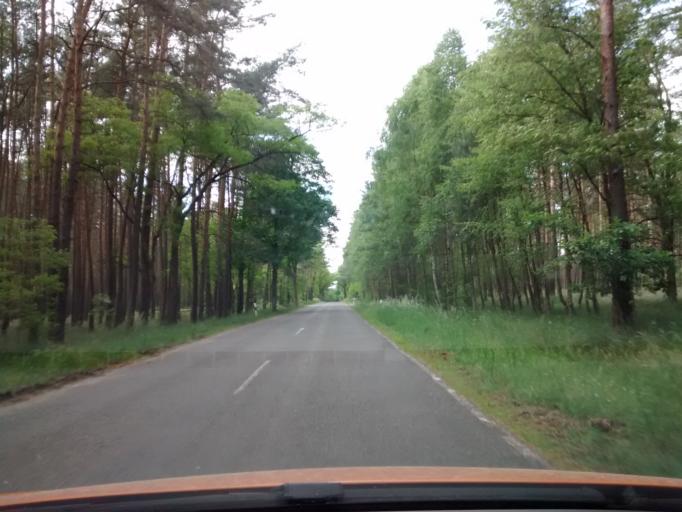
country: DE
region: Brandenburg
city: Ihlow
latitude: 51.9695
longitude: 13.3136
